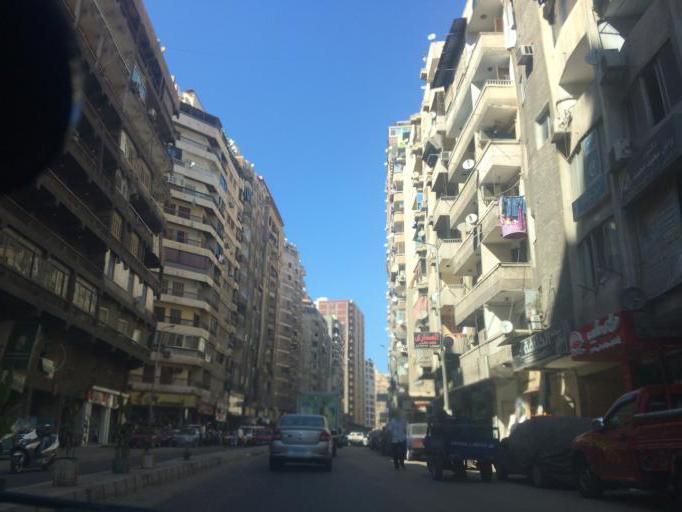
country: EG
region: Alexandria
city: Alexandria
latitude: 31.2705
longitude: 30.0020
